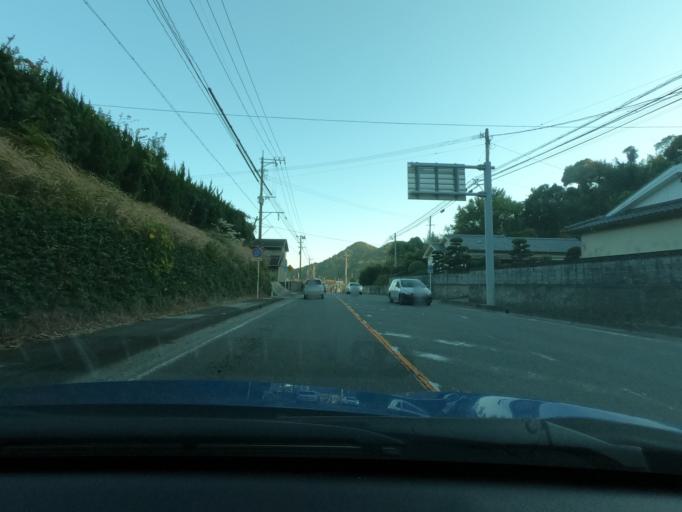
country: JP
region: Kagoshima
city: Satsumasendai
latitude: 31.8575
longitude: 130.2321
